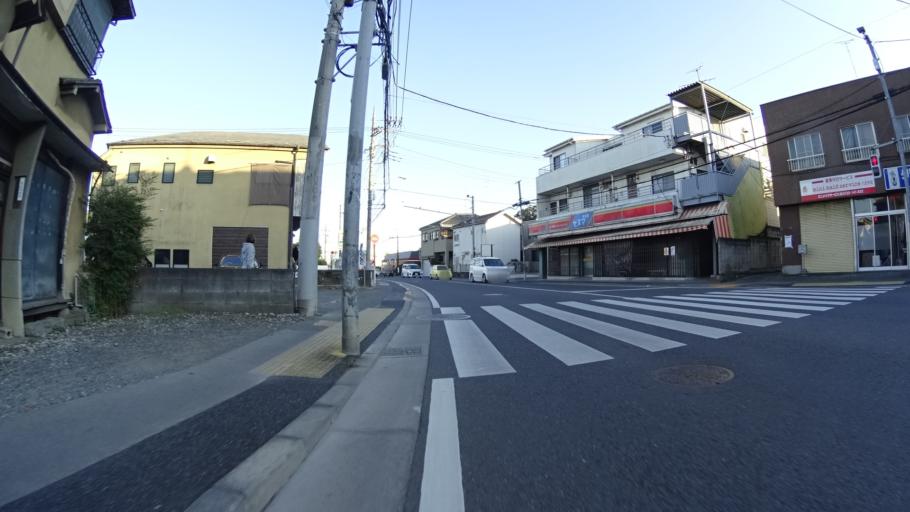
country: JP
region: Tokyo
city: Hachioji
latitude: 35.6643
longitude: 139.3051
